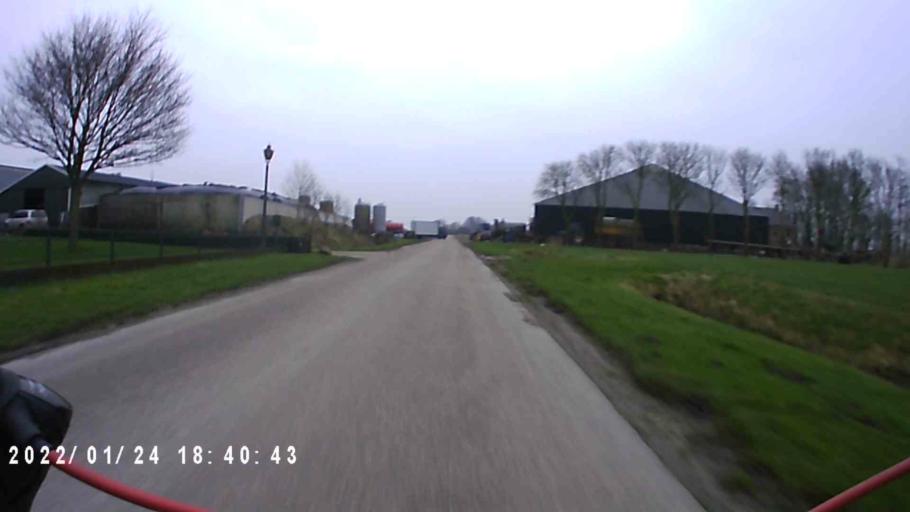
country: NL
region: Groningen
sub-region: Gemeente De Marne
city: Ulrum
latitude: 53.3459
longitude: 6.3469
